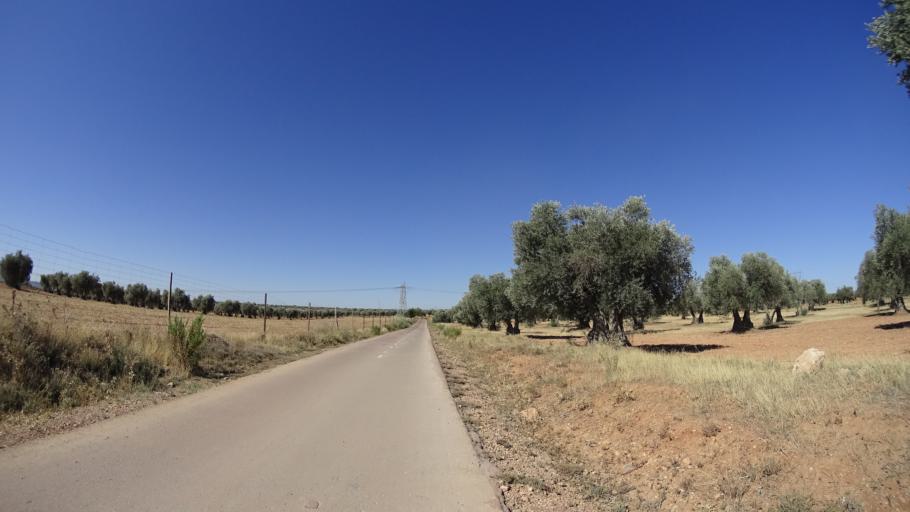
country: ES
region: Madrid
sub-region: Provincia de Madrid
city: Morata de Tajuna
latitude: 40.2397
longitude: -3.4745
